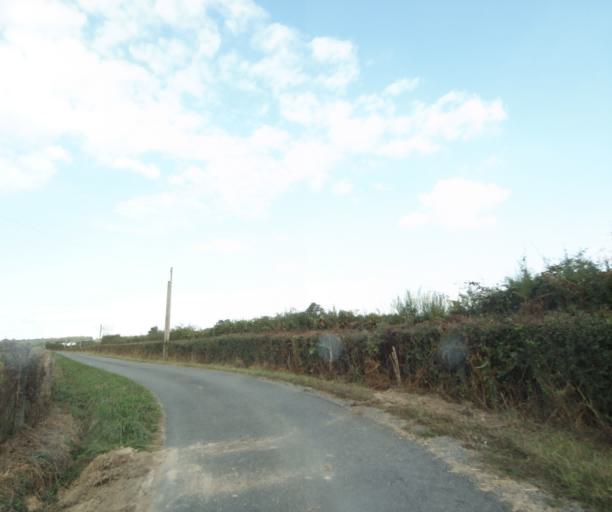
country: FR
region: Bourgogne
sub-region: Departement de Saone-et-Loire
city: Palinges
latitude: 46.5626
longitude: 4.1897
